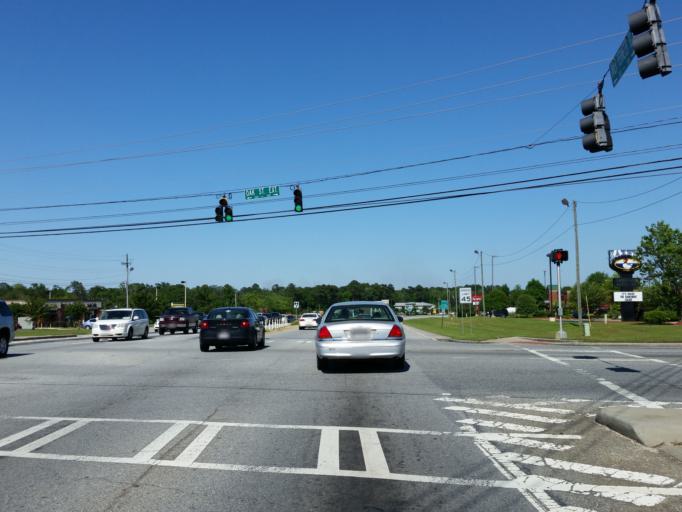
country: US
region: Georgia
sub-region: Lowndes County
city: Remerton
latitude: 30.8822
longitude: -83.2918
